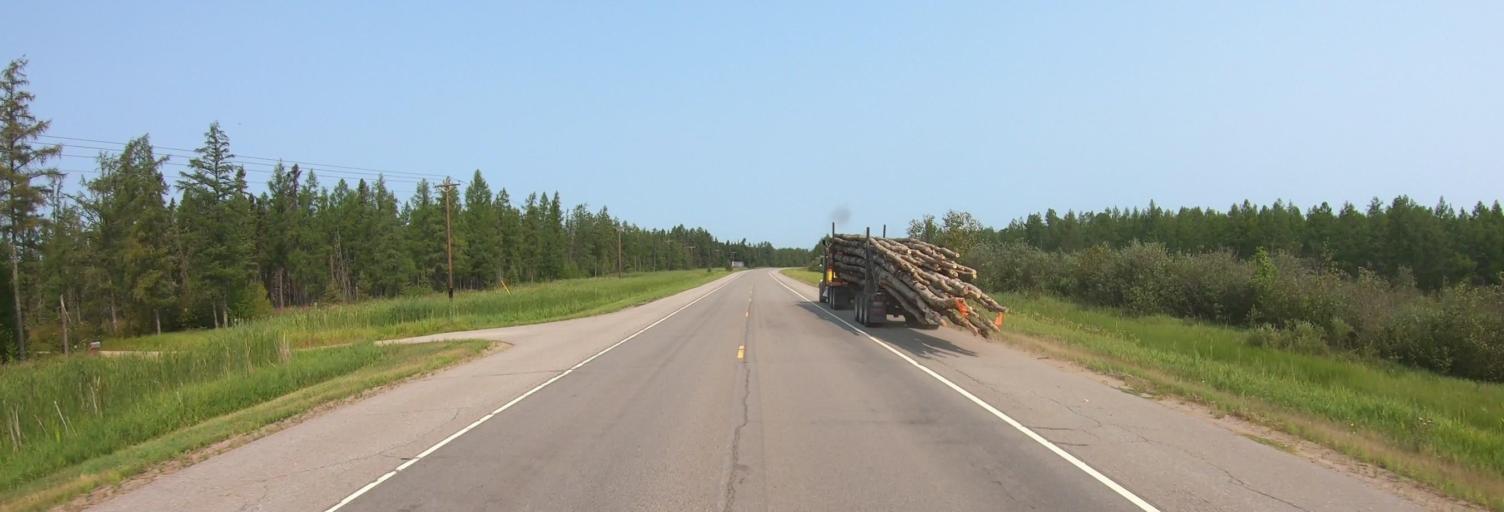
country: US
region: Minnesota
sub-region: Saint Louis County
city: Mountain Iron
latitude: 48.0370
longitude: -92.8322
